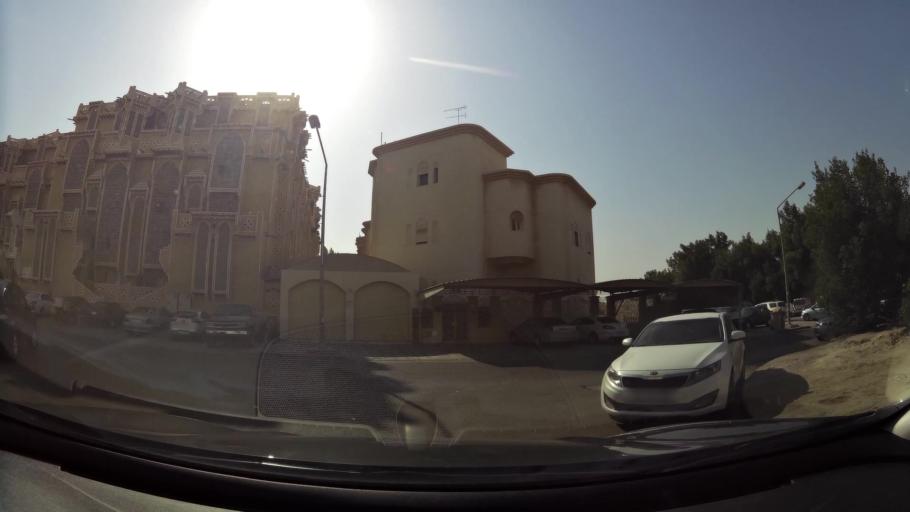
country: KW
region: Muhafazat Hawalli
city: Salwa
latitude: 29.2891
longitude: 48.0743
